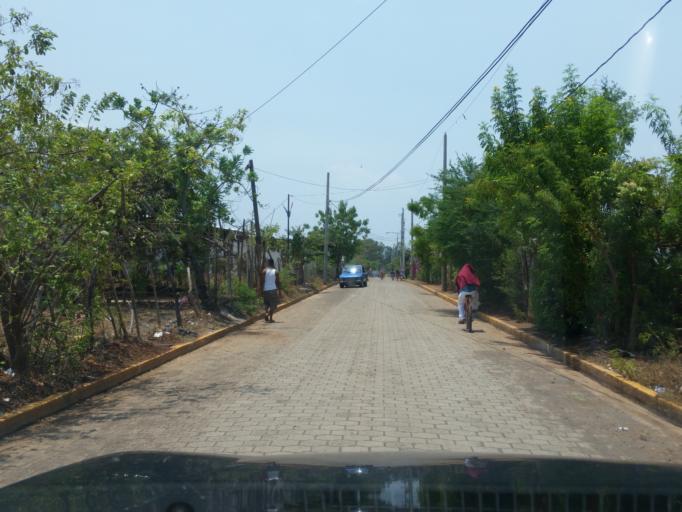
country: NI
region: Granada
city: Granada
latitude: 11.9098
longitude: -85.9608
